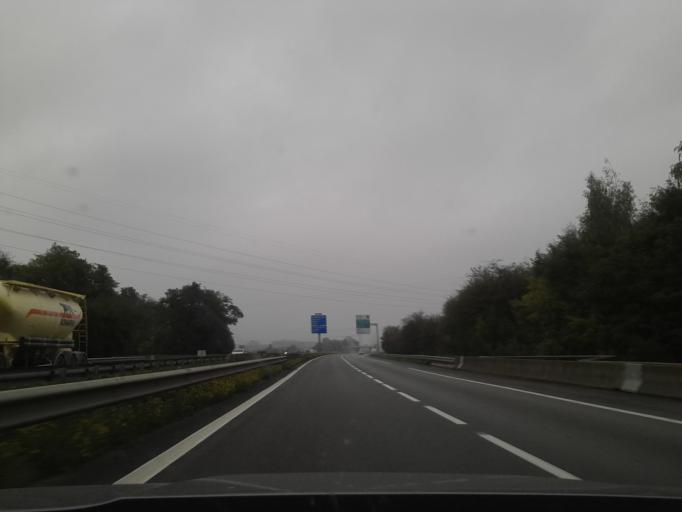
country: FR
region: Nord-Pas-de-Calais
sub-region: Departement du Nord
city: Hordain
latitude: 50.2591
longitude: 3.3272
